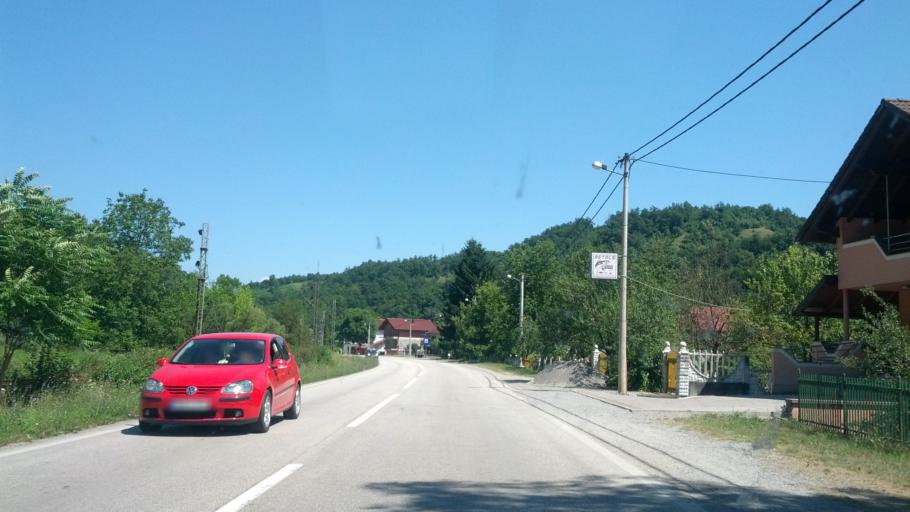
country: BA
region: Federation of Bosnia and Herzegovina
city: Bosanska Krupa
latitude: 44.9034
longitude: 16.1635
